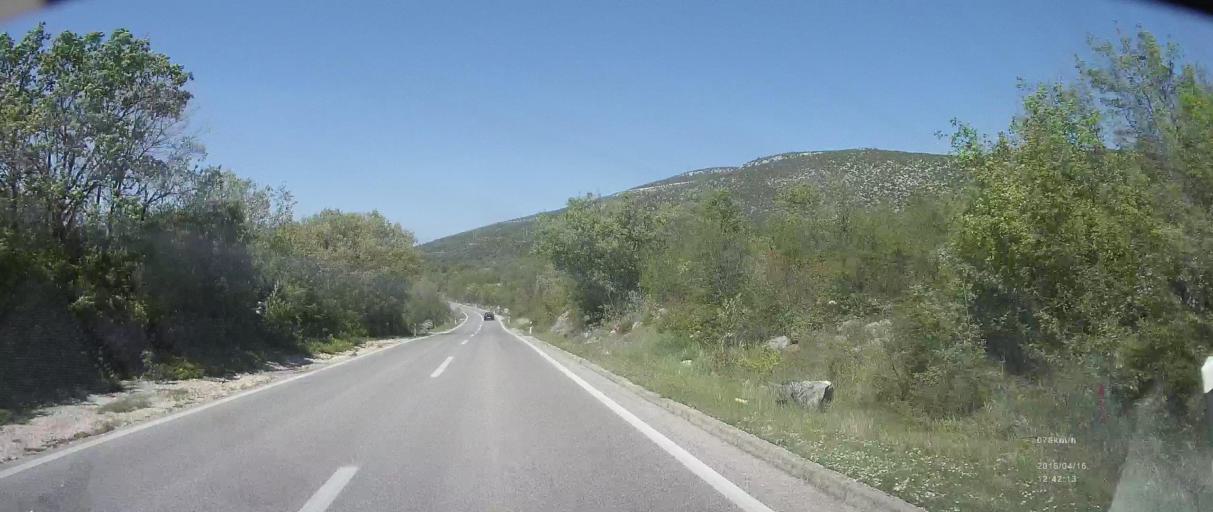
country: HR
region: Sibensko-Kniniska
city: Rogoznica
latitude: 43.6275
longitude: 16.0921
